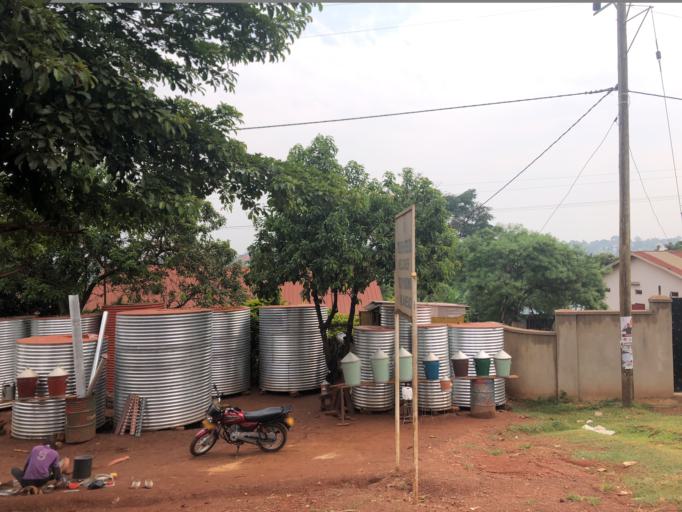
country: UG
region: Central Region
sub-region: Mukono District
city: Mukono
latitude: 0.3709
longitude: 32.7357
